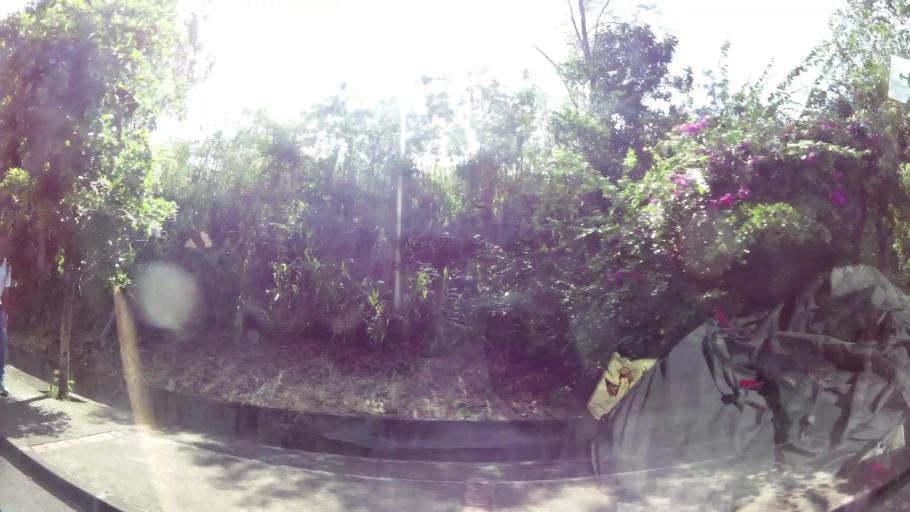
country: GP
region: Guadeloupe
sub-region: Guadeloupe
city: Basse-Terre
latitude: 16.0029
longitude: -61.7272
